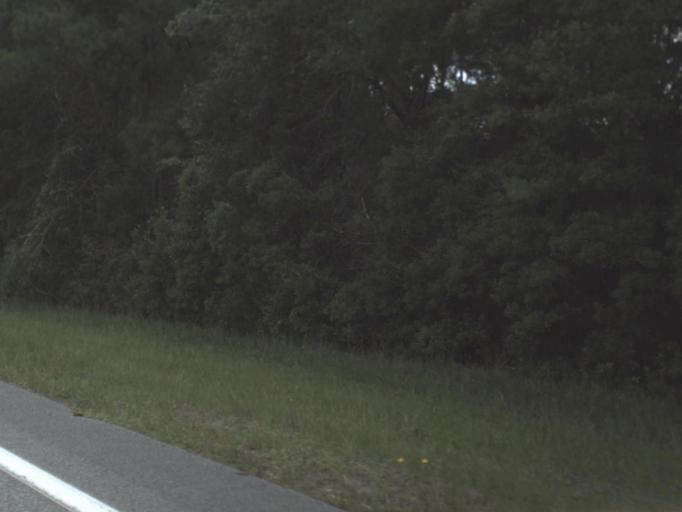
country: US
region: Florida
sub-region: Levy County
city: Bronson
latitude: 29.3662
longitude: -82.7243
